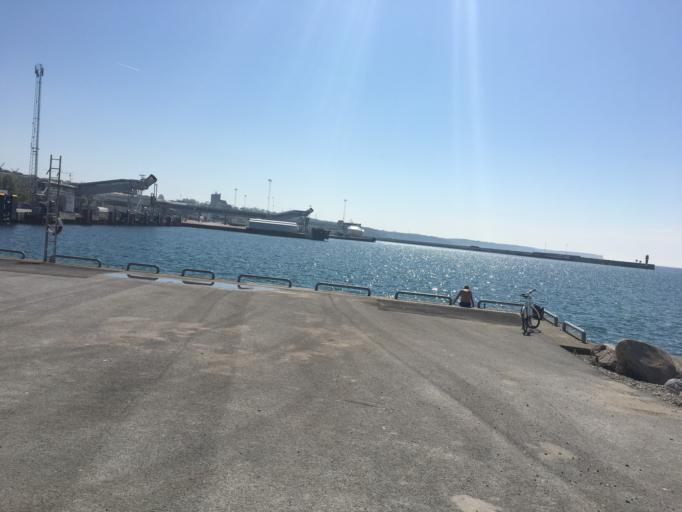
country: SE
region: Gotland
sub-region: Gotland
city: Visby
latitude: 57.6376
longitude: 18.2806
